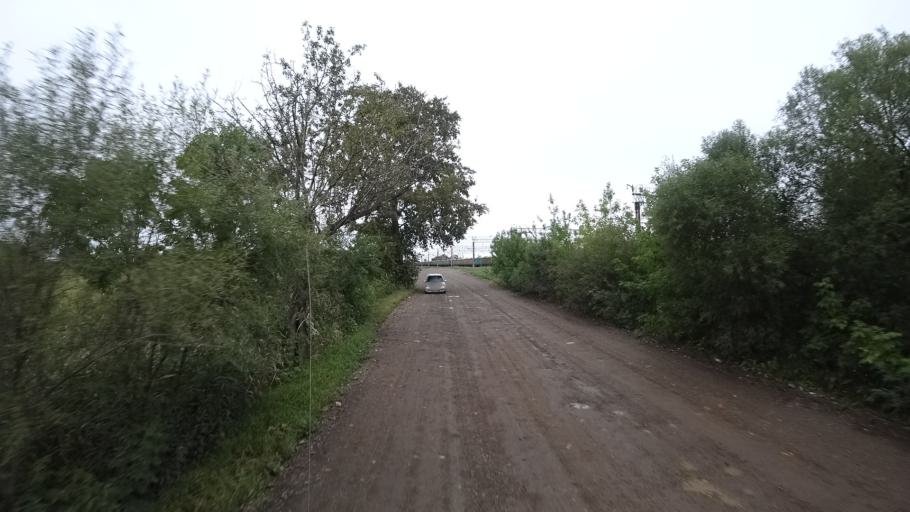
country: RU
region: Primorskiy
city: Chernigovka
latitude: 44.3377
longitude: 132.5289
